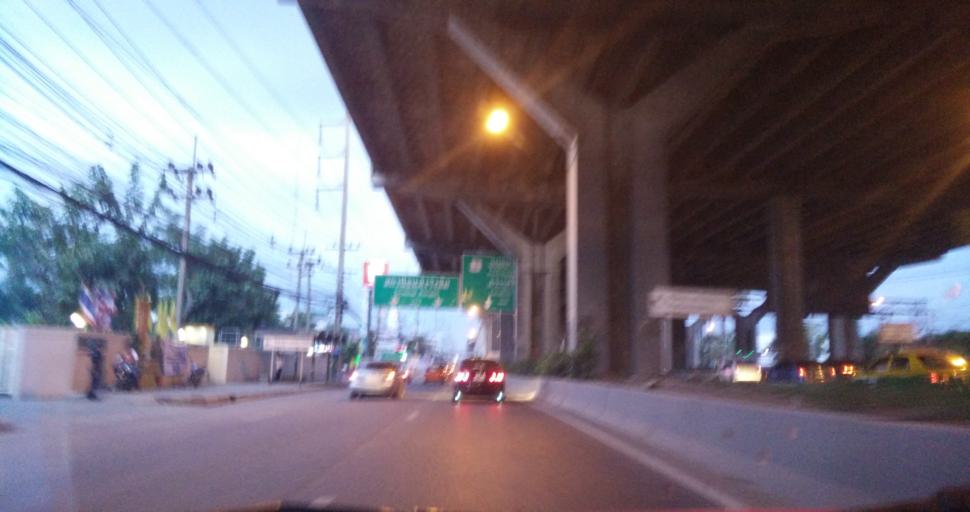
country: TH
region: Phra Nakhon Si Ayutthaya
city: Ban Bang Kadi Pathum Thani
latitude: 13.9977
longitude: 100.6146
